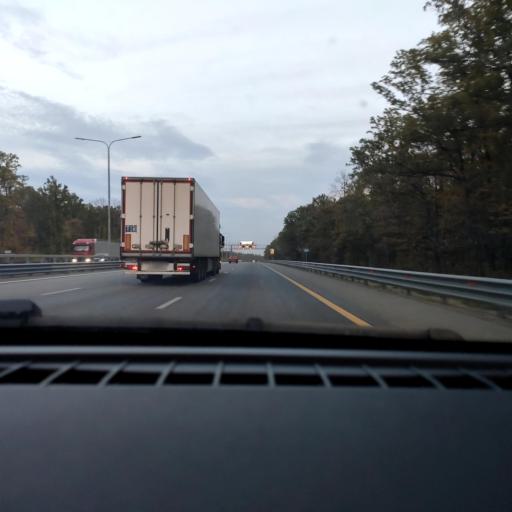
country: RU
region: Voronezj
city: Podgornoye
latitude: 51.8346
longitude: 39.2297
